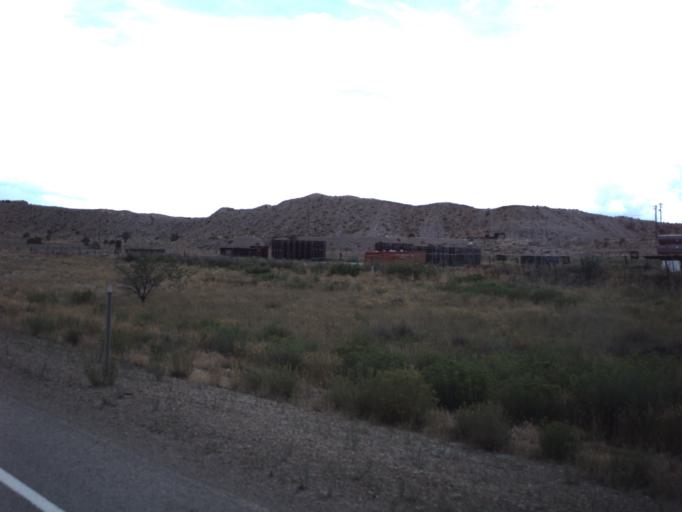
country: US
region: Utah
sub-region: Carbon County
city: Price
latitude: 39.5497
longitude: -110.8159
